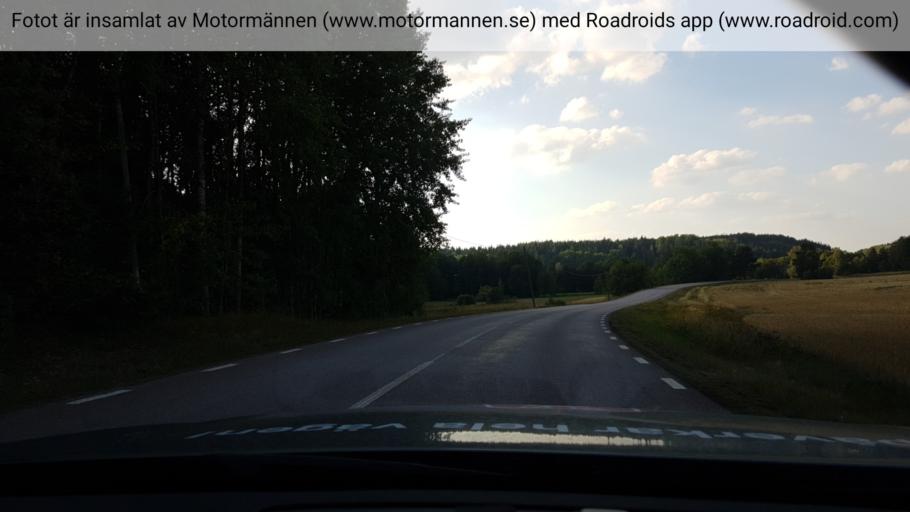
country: SE
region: Soedermanland
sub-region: Strangnas Kommun
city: Mariefred
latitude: 59.2213
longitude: 17.1670
